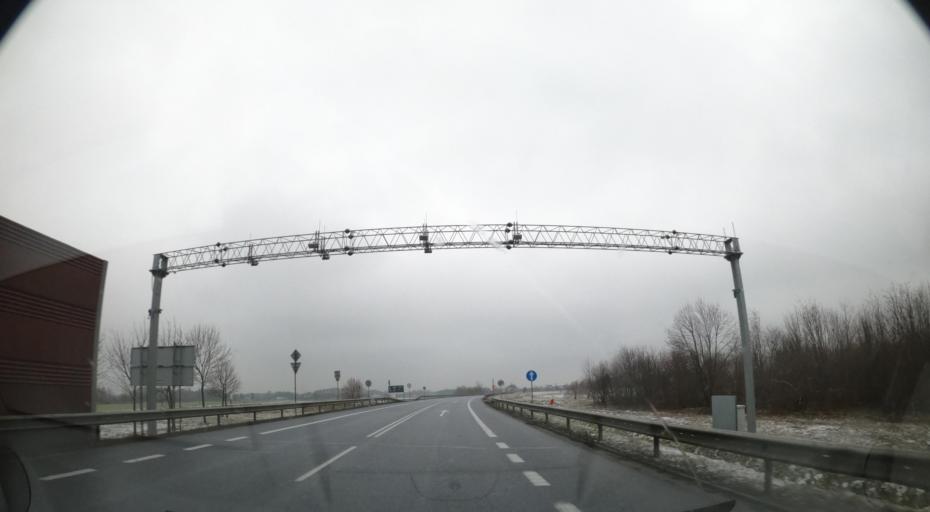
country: PL
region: Masovian Voivodeship
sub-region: Powiat sochaczewski
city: Sochaczew
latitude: 52.2082
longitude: 20.2477
